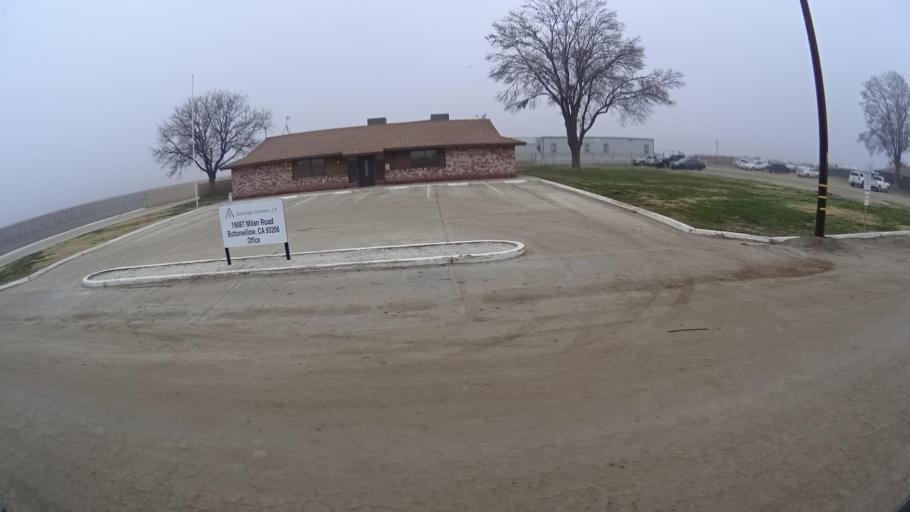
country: US
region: California
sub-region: Kern County
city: Buttonwillow
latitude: 35.4572
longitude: -119.5649
